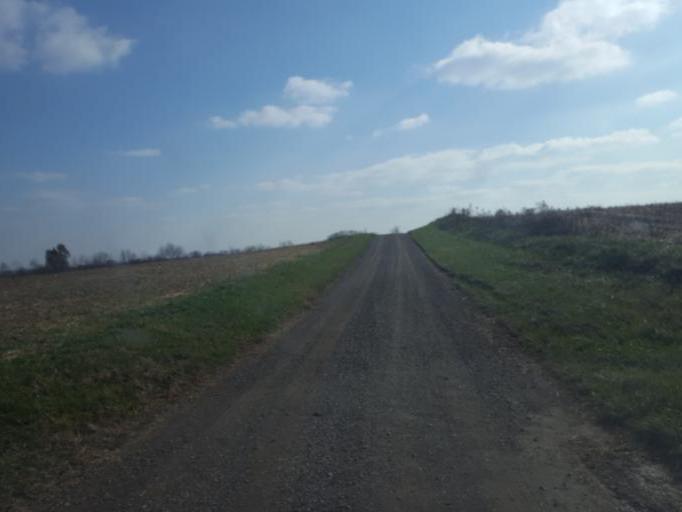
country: US
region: Ohio
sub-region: Knox County
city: Oak Hill
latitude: 40.3788
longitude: -82.1381
